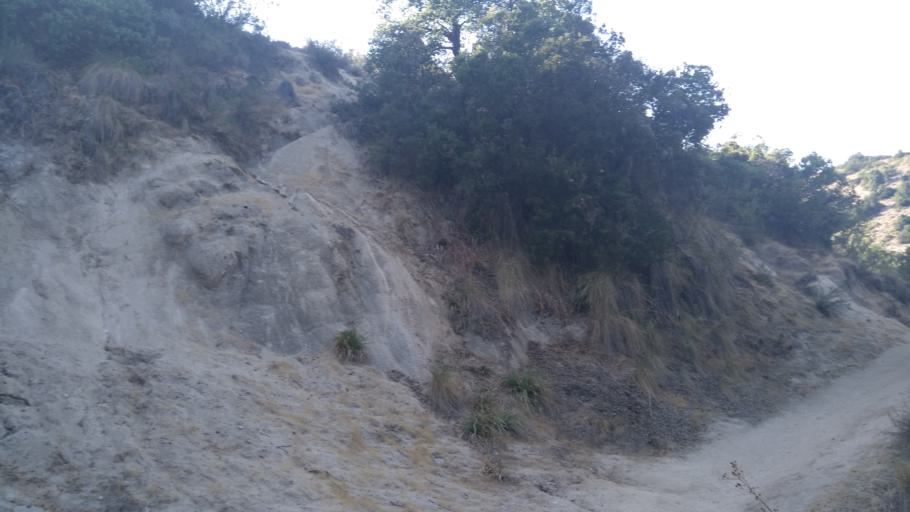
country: CL
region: Santiago Metropolitan
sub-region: Provincia de Cordillera
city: Puente Alto
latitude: -33.7257
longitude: -70.4732
